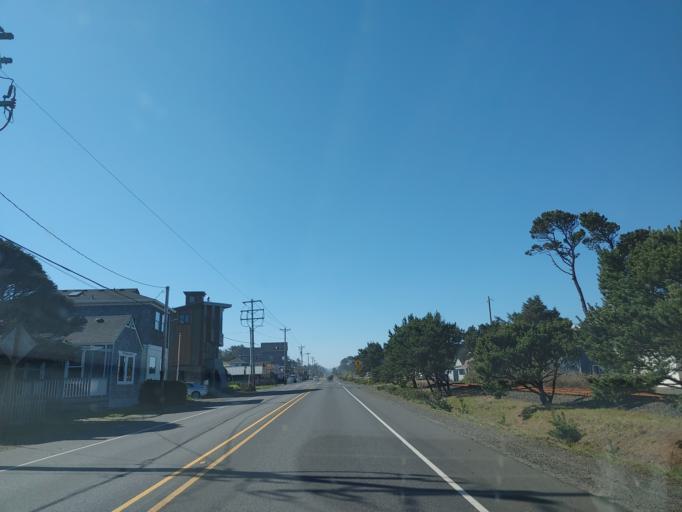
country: US
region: Oregon
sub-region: Tillamook County
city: Rockaway Beach
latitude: 45.6086
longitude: -123.9447
